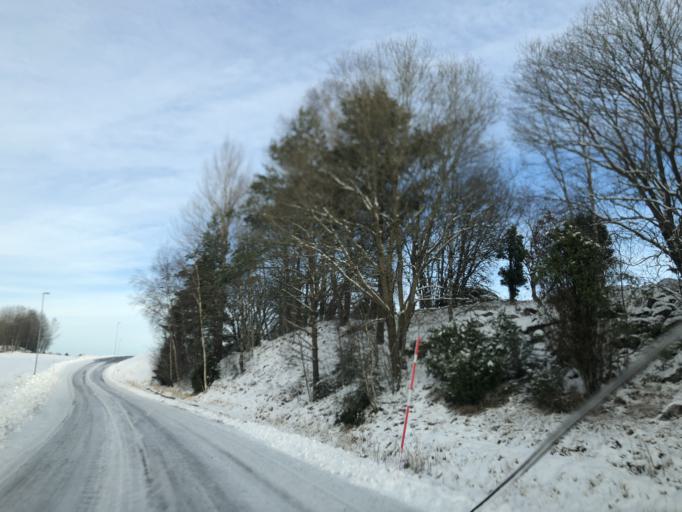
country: SE
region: Vaestra Goetaland
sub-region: Ulricehamns Kommun
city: Ulricehamn
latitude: 57.7920
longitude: 13.5327
